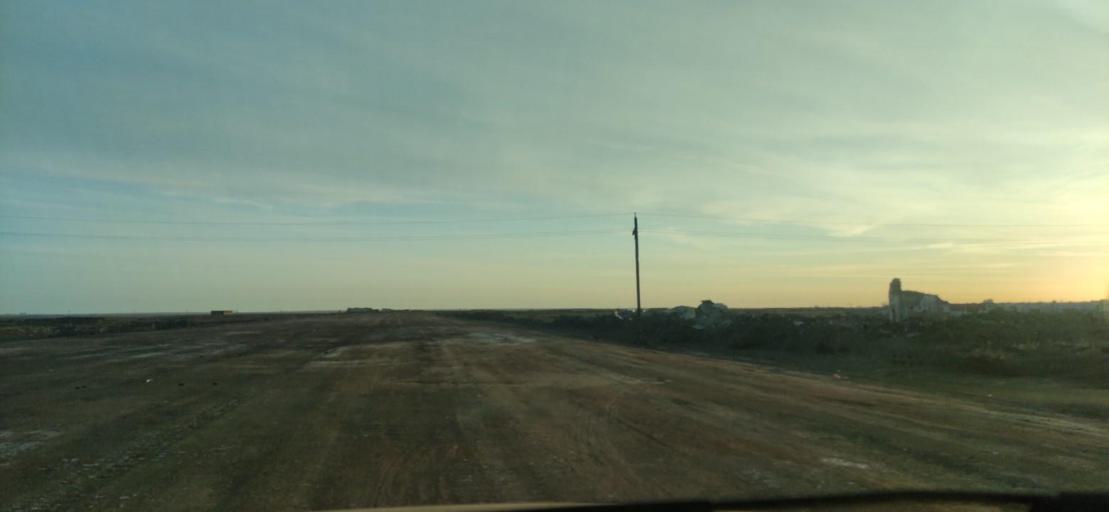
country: KZ
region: Qaraghandy
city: Saryshaghan
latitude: 46.0194
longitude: 73.5895
